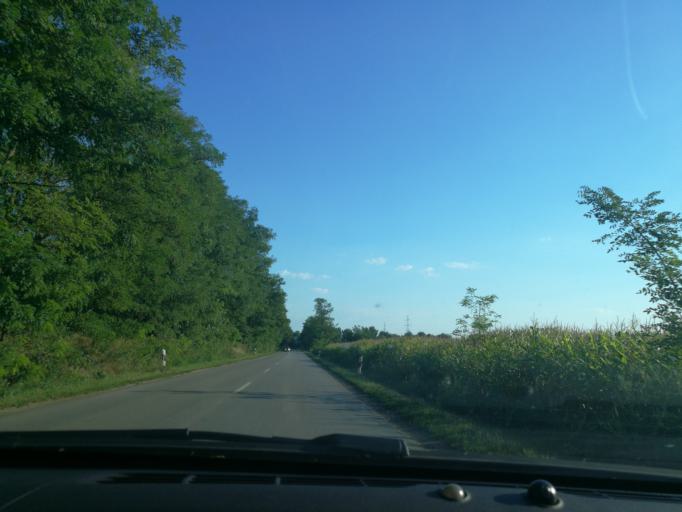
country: HU
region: Szabolcs-Szatmar-Bereg
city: Buj
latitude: 48.0883
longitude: 21.6410
